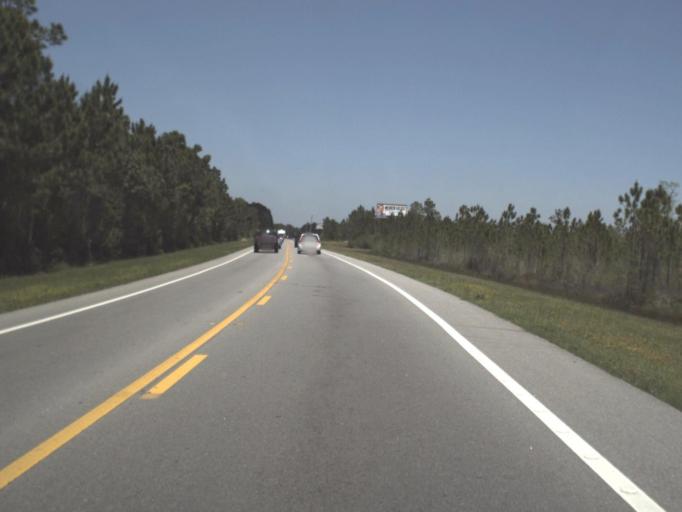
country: US
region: Florida
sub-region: Escambia County
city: Myrtle Grove
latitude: 30.3942
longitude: -87.3428
